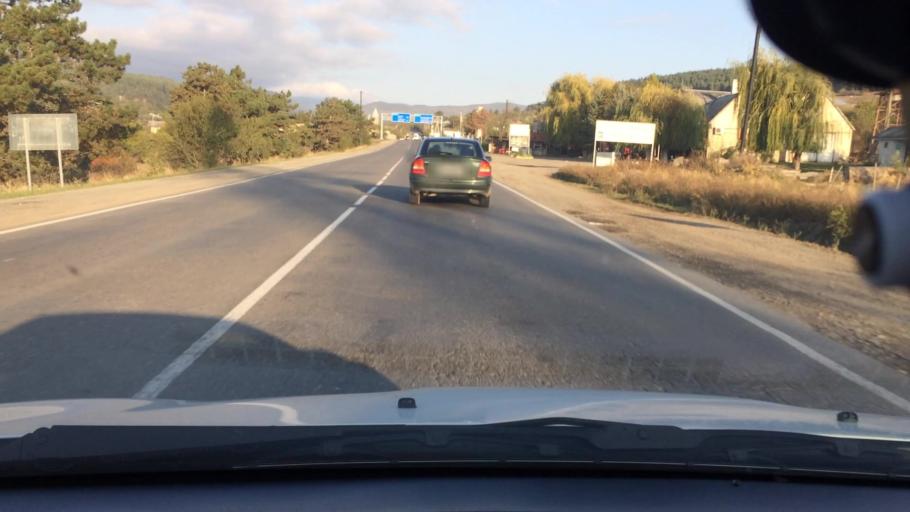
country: GE
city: Surami
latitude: 42.0129
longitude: 43.5766
